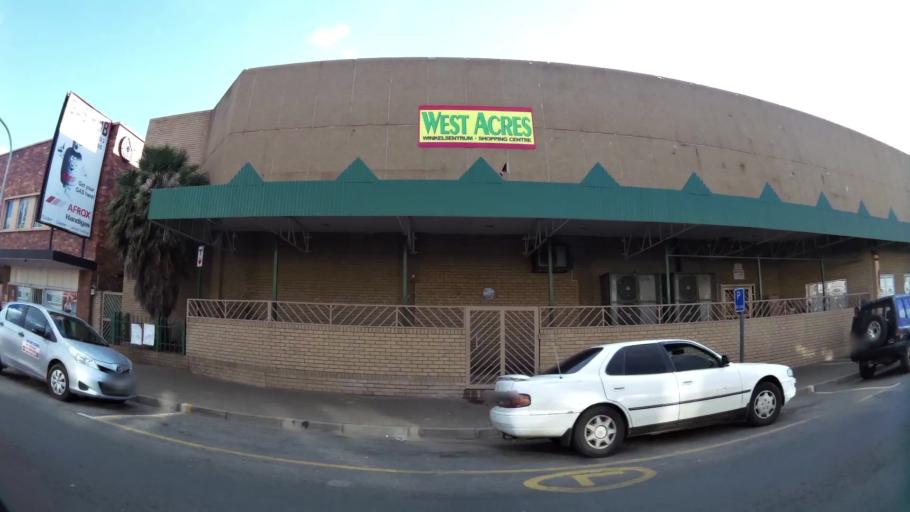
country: ZA
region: North-West
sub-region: Dr Kenneth Kaunda District Municipality
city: Potchefstroom
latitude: -26.7090
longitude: 27.0975
